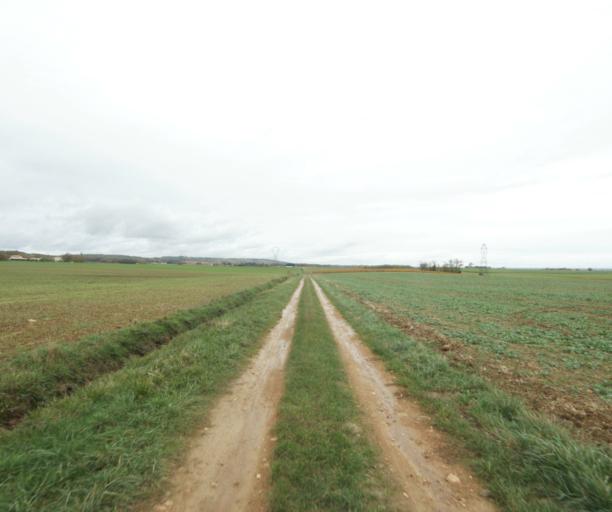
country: FR
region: Bourgogne
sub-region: Departement de Saone-et-Loire
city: Saint-Martin-Belle-Roche
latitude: 46.4641
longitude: 4.8540
